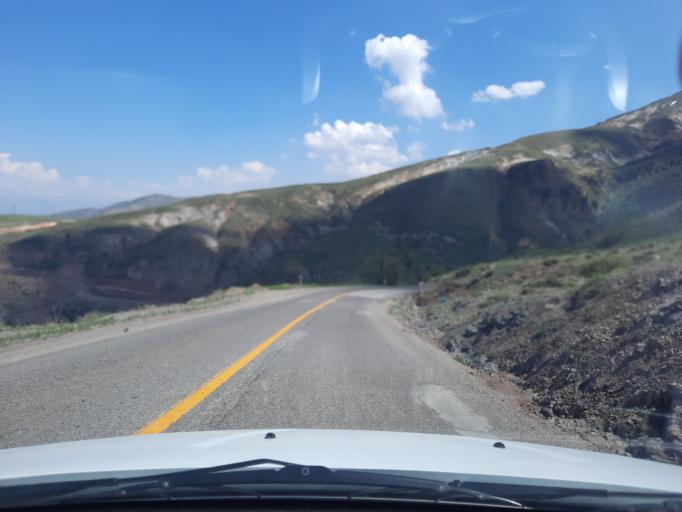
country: IR
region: Qazvin
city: Qazvin
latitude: 36.4058
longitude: 50.2232
